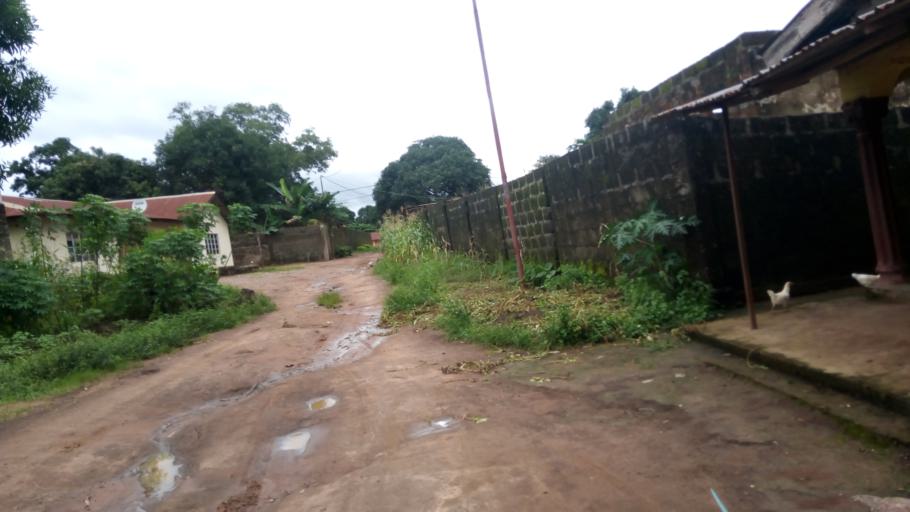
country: SL
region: Northern Province
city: Lunsar
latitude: 8.6919
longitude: -12.5288
